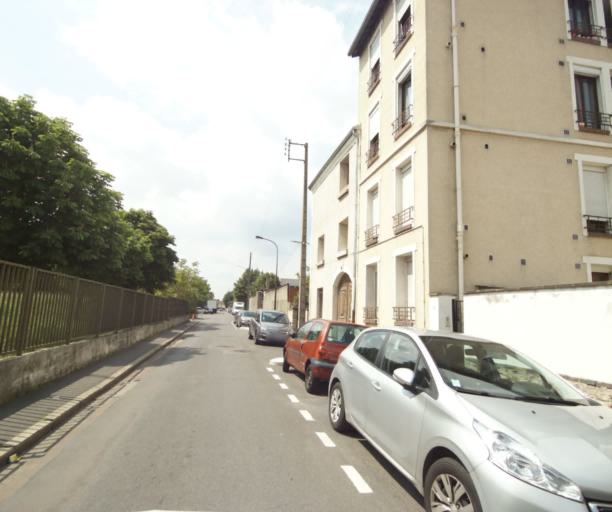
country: FR
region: Ile-de-France
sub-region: Departement du Val-d'Oise
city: Argenteuil
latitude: 48.9375
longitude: 2.2440
